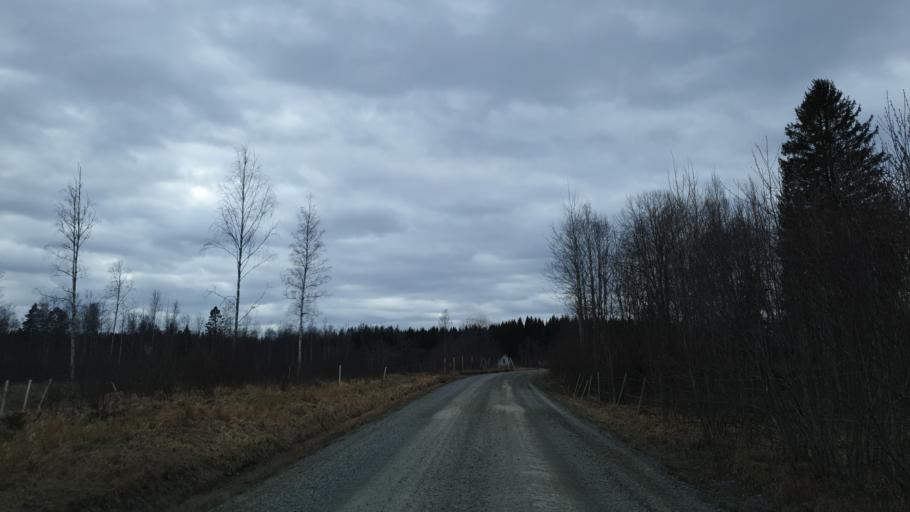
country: SE
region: OErebro
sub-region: Nora Kommun
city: As
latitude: 59.6008
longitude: 14.9104
